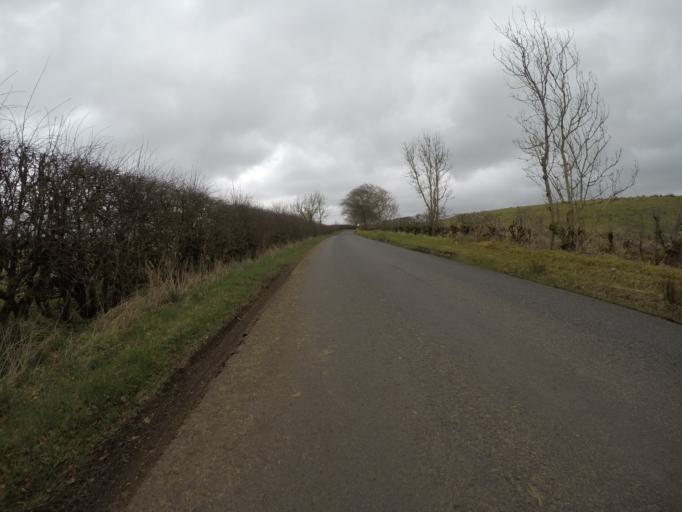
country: GB
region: Scotland
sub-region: East Ayrshire
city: Stewarton
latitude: 55.6804
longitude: -4.4479
